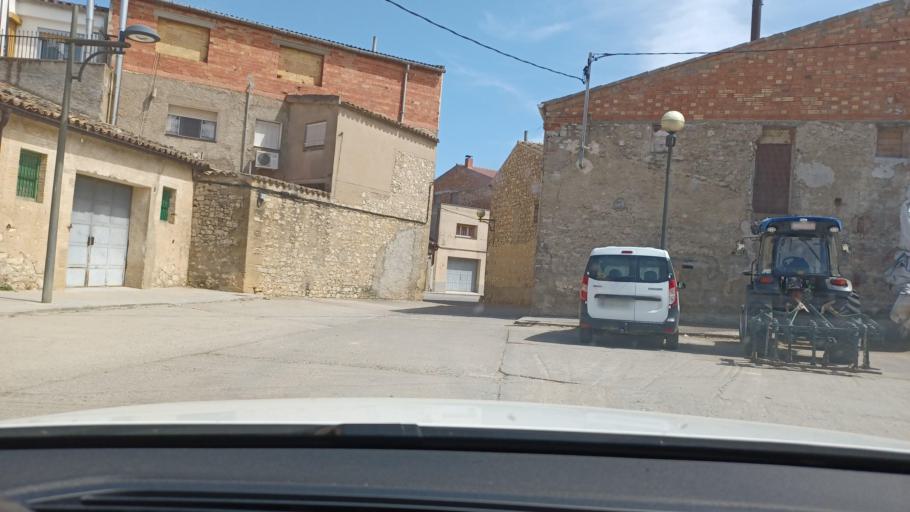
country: ES
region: Catalonia
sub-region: Provincia de Tarragona
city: Vilalba dels Arcs
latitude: 41.1192
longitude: 0.4085
